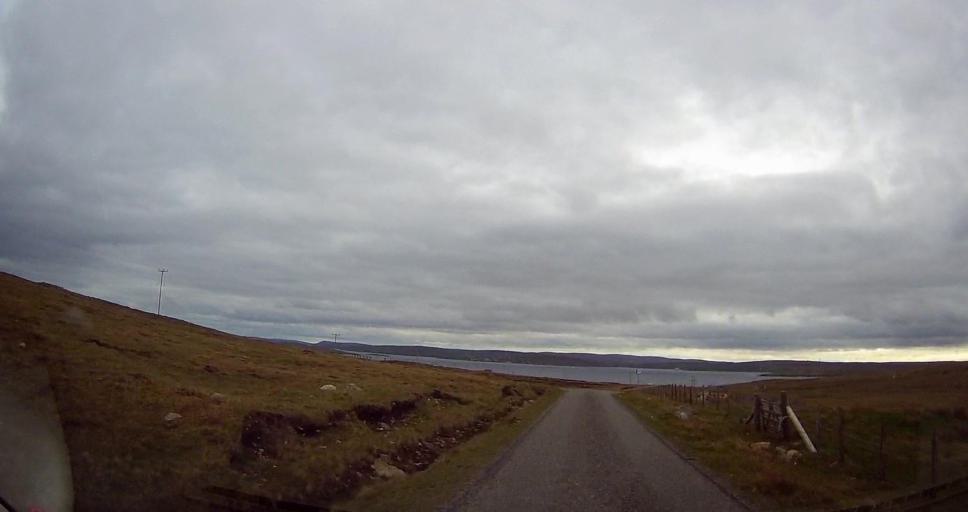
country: GB
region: Scotland
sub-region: Shetland Islands
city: Shetland
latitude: 60.5033
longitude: -1.1480
